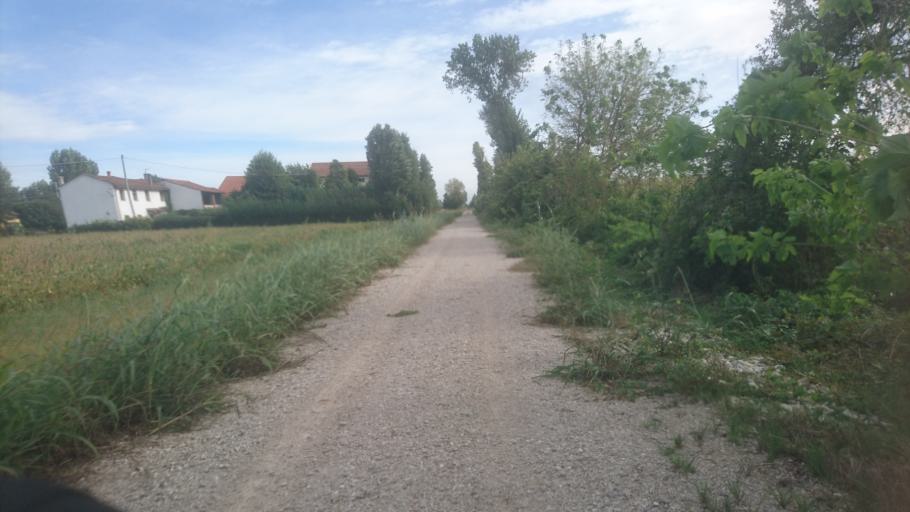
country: IT
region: Veneto
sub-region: Provincia di Vicenza
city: Montegalda
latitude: 45.4679
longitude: 11.6569
